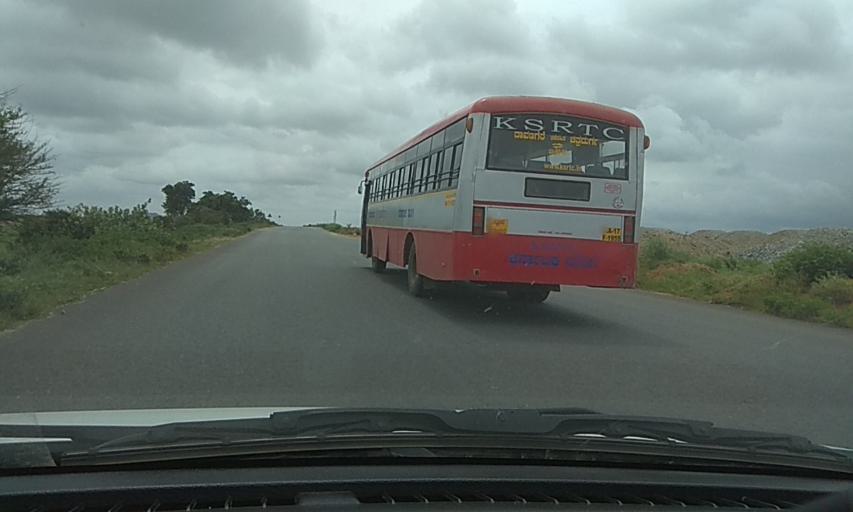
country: IN
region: Karnataka
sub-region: Chitradurga
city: Chitradurga
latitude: 14.2851
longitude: 76.2988
